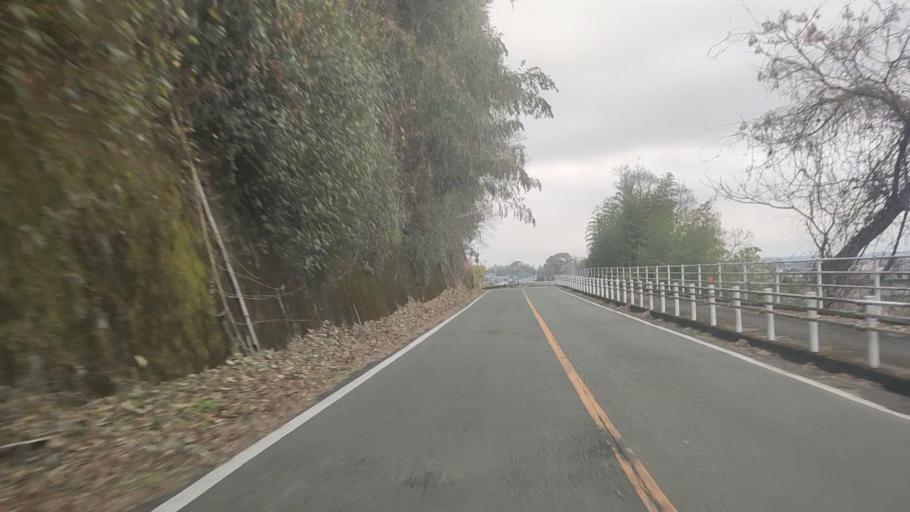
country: JP
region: Kumamoto
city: Ozu
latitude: 32.8524
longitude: 130.8666
